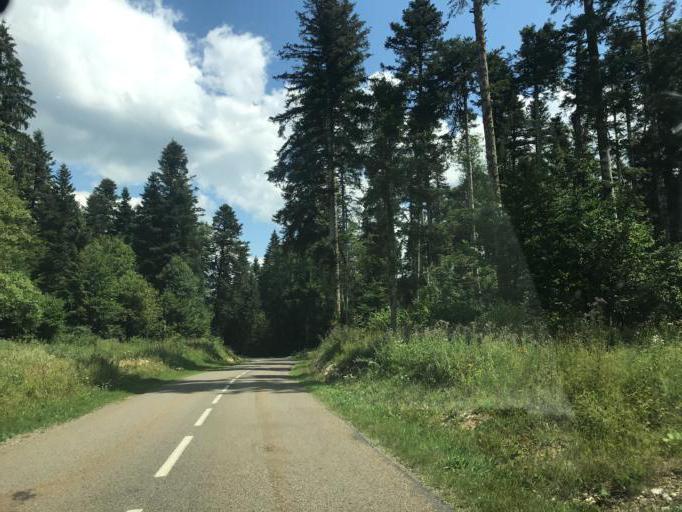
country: FR
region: Franche-Comte
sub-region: Departement du Jura
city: Clairvaux-les-Lacs
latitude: 46.5186
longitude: 5.7905
